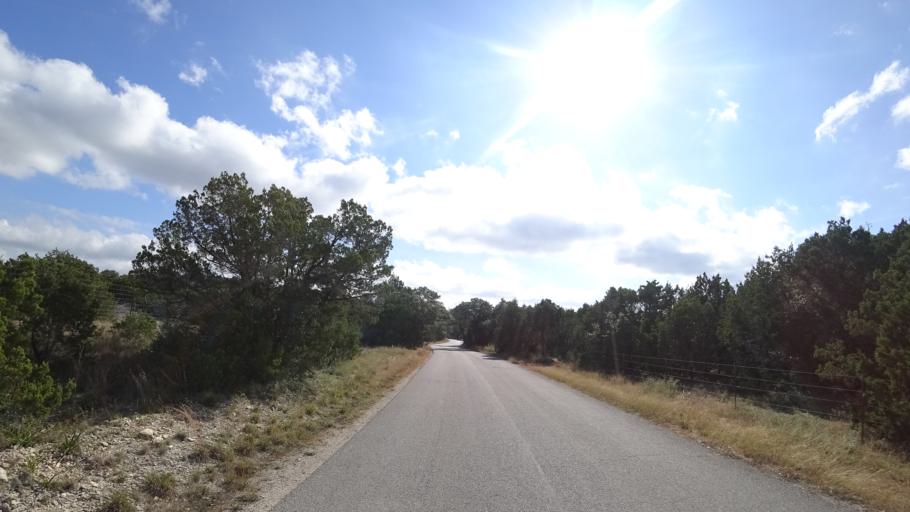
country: US
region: Texas
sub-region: Travis County
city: Bee Cave
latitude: 30.2579
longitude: -97.9370
